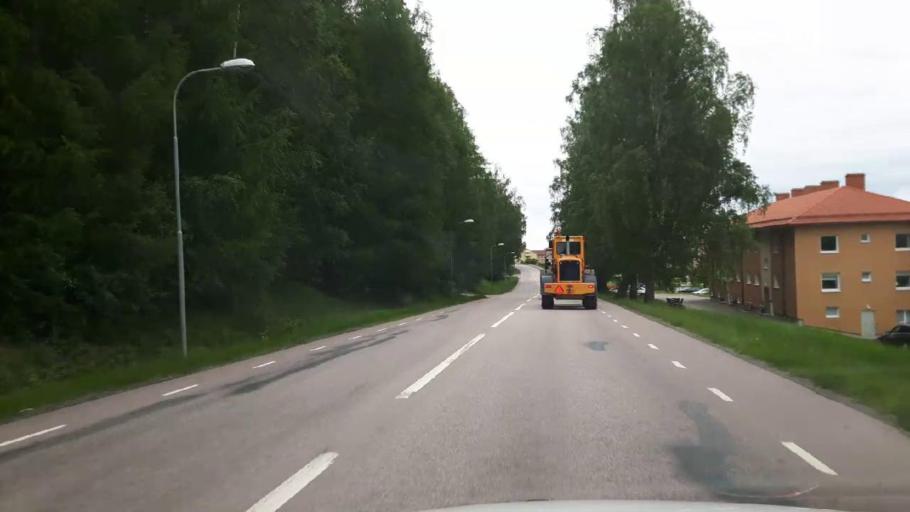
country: SE
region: Vaestmanland
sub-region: Kopings Kommun
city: Kolsva
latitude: 59.6062
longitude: 15.8321
